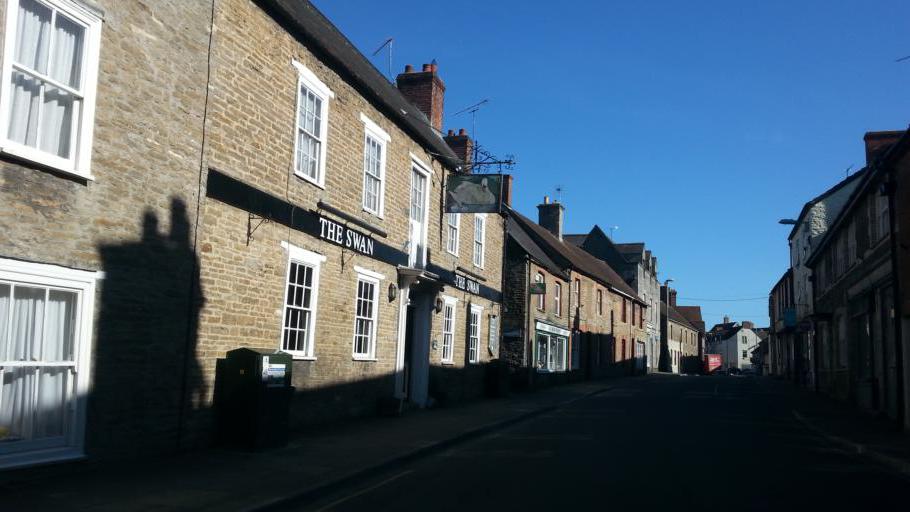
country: GB
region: England
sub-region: Dorset
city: Stalbridge
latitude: 50.9607
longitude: -2.3787
